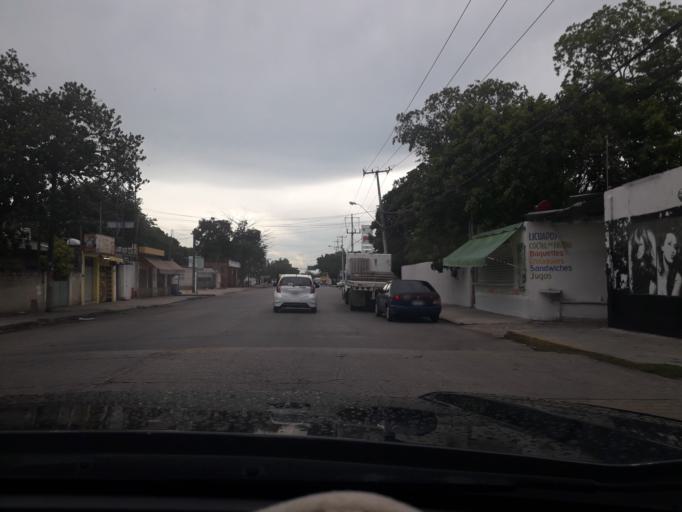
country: MX
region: Yucatan
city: Merida
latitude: 20.9509
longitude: -89.6500
